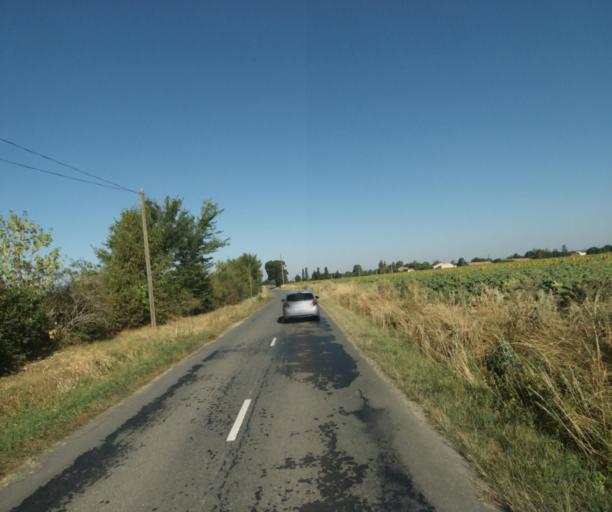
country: FR
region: Midi-Pyrenees
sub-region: Departement de la Haute-Garonne
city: Revel
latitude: 43.4788
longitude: 2.0113
